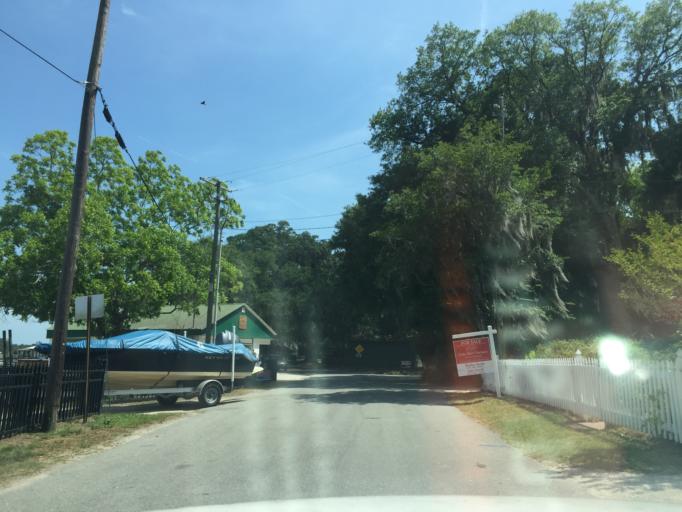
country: US
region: Georgia
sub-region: Chatham County
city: Isle of Hope
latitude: 31.9800
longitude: -81.0571
